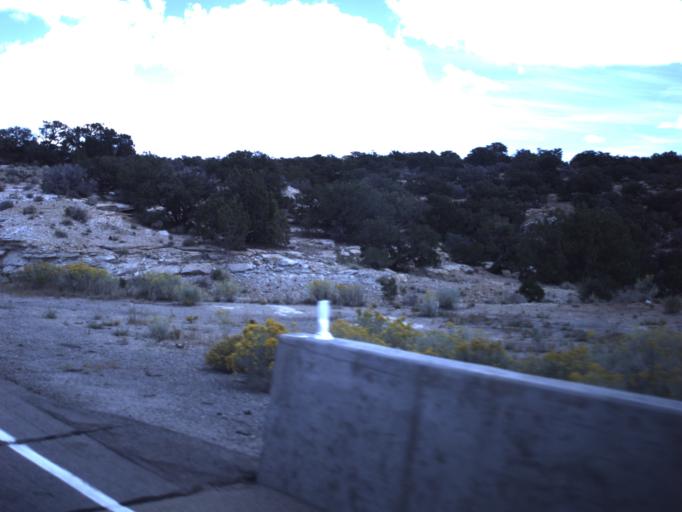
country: US
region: Utah
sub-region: Emery County
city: Ferron
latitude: 38.8603
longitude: -110.8643
